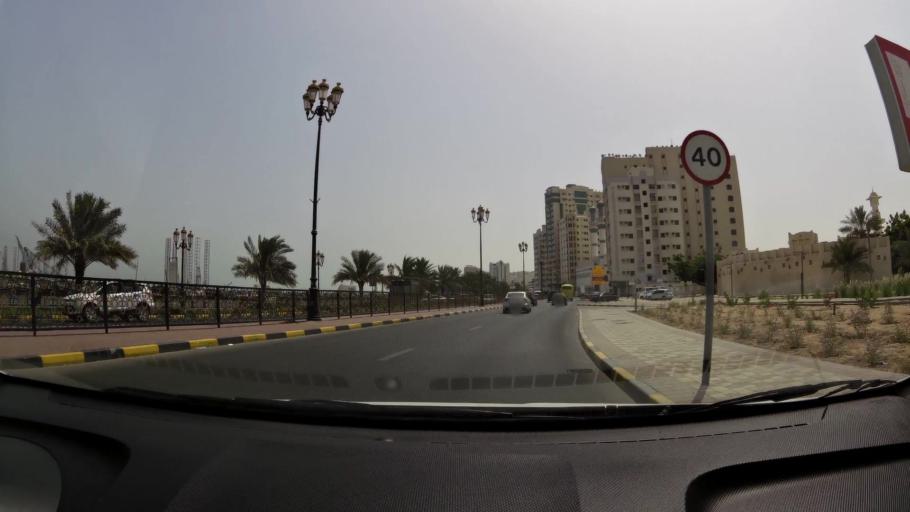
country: AE
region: Ash Shariqah
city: Sharjah
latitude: 25.3574
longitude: 55.3798
